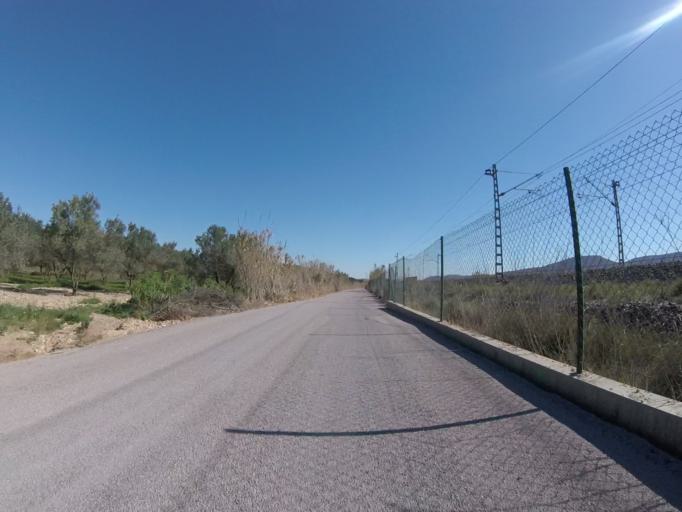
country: ES
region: Valencia
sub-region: Provincia de Castello
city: Alcala de Xivert
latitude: 40.3389
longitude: 0.2589
